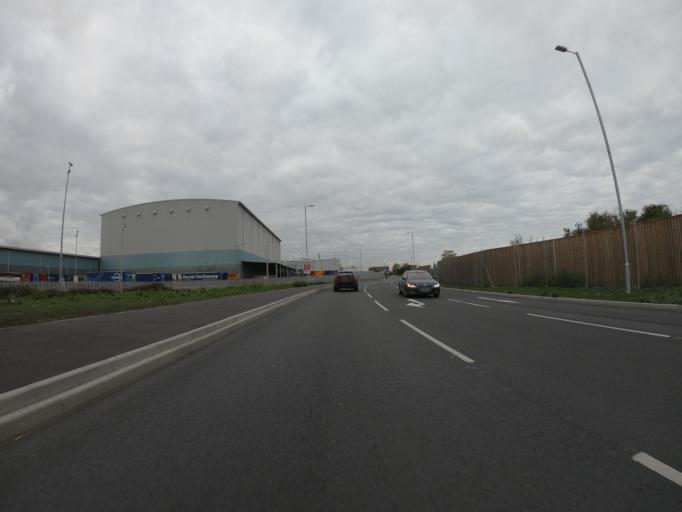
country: GB
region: England
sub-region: Borough of Thurrock
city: Tilbury
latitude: 51.4569
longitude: 0.3636
